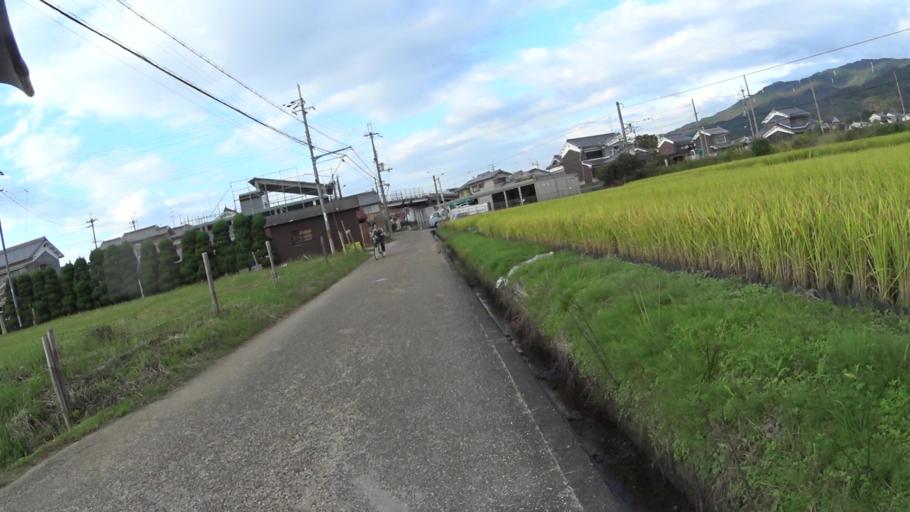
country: JP
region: Nara
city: Tenri
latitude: 34.5423
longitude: 135.8415
